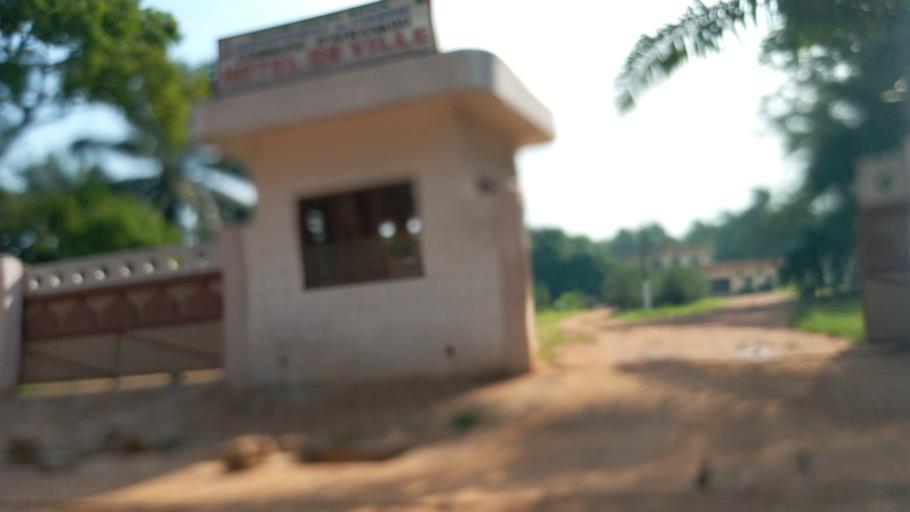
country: BJ
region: Queme
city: Porto-Novo
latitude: 6.5554
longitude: 2.6620
